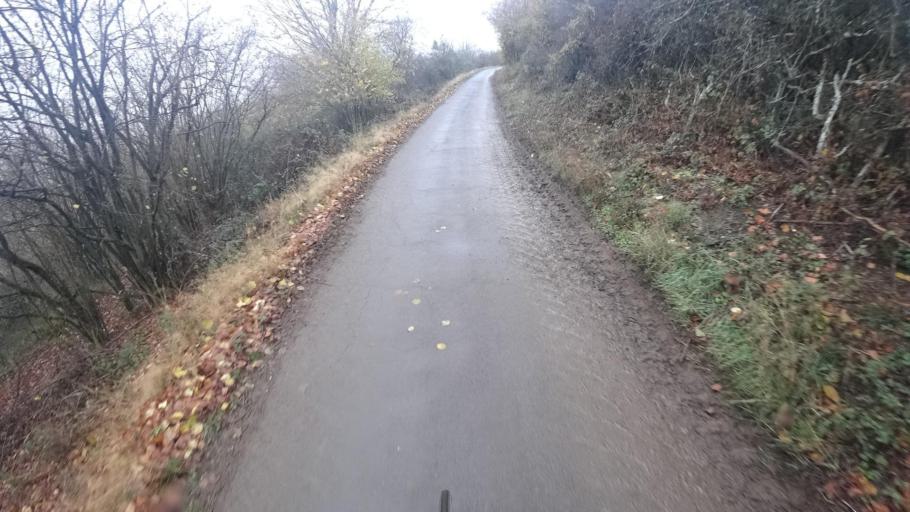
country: DE
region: Rheinland-Pfalz
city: Kesseling
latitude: 50.4942
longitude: 7.0142
